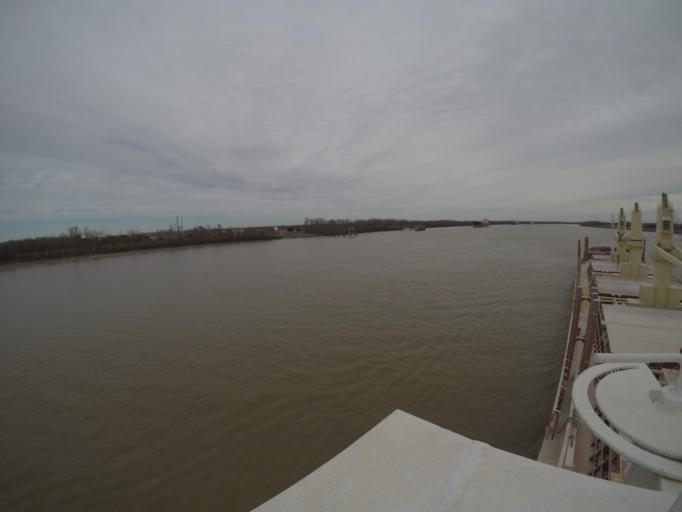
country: US
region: Louisiana
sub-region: Saint John the Baptist Parish
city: Reserve
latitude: 30.0471
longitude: -90.5252
